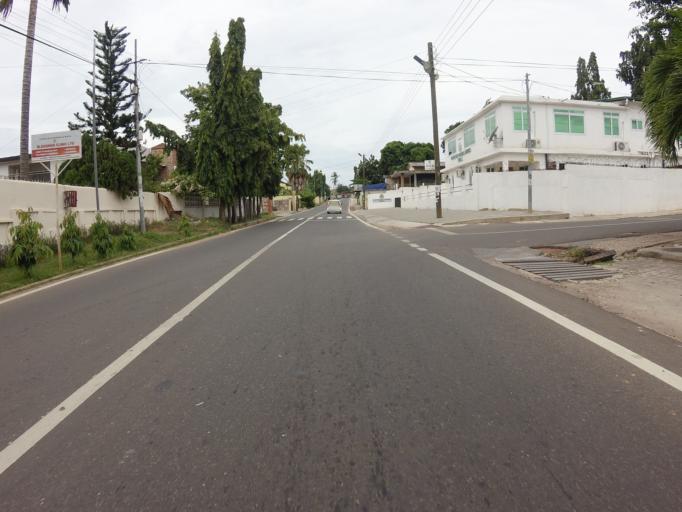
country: GH
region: Greater Accra
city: Dome
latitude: 5.6007
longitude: -0.2308
